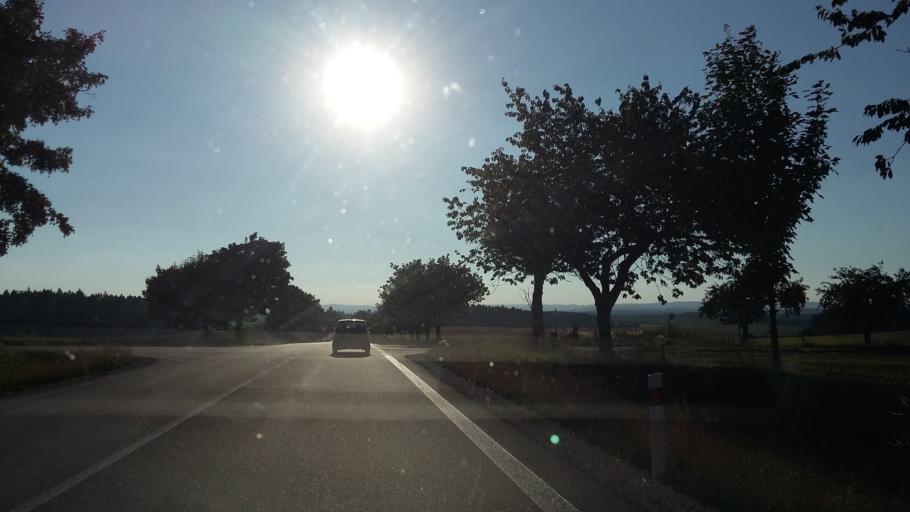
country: CZ
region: Vysocina
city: Kamenice
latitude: 49.3972
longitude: 15.7676
